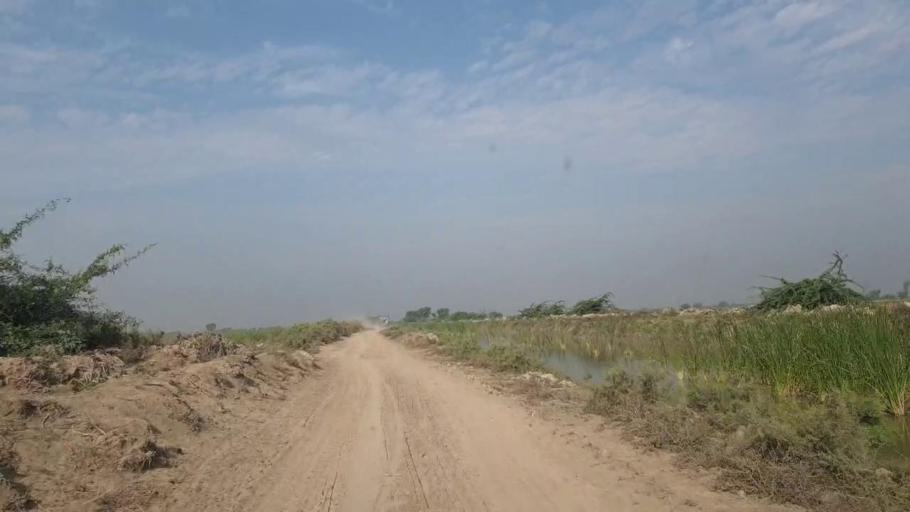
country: PK
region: Sindh
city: Tando Bago
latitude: 24.8734
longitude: 68.9636
